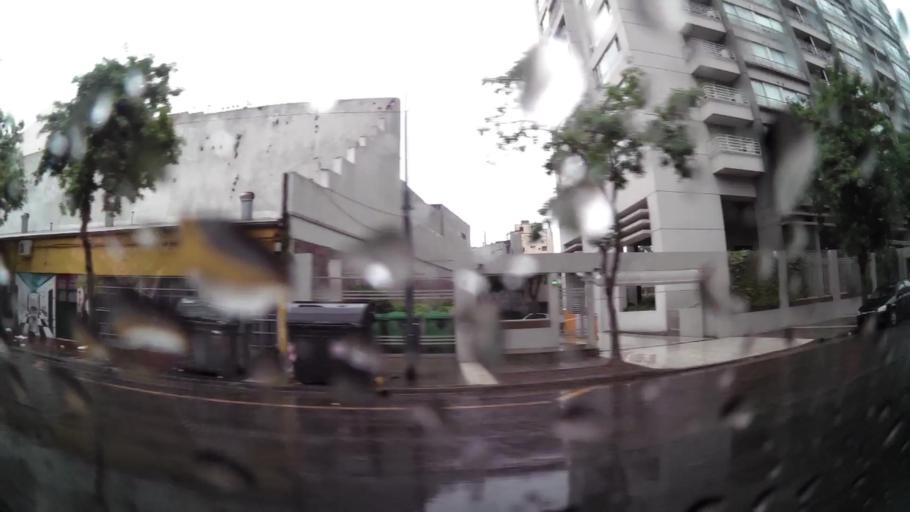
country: AR
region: Buenos Aires F.D.
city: Buenos Aires
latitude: -34.6248
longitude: -58.3763
